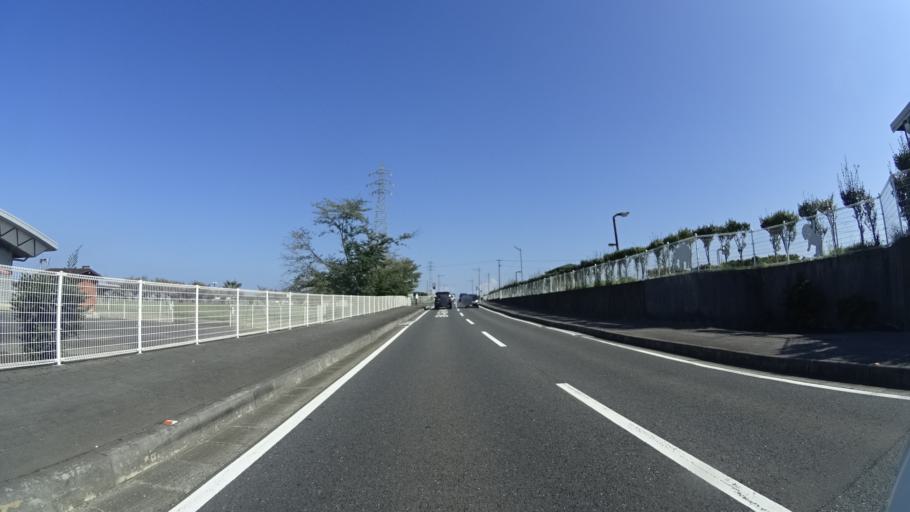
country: JP
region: Fukuoka
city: Tsuiki
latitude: 33.6638
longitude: 131.0309
